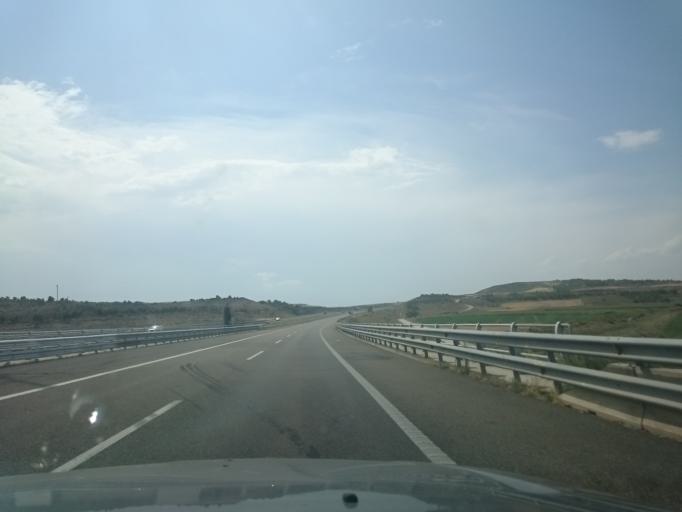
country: ES
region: Aragon
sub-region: Provincia de Huesca
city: Penalba
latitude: 41.5131
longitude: -0.0378
